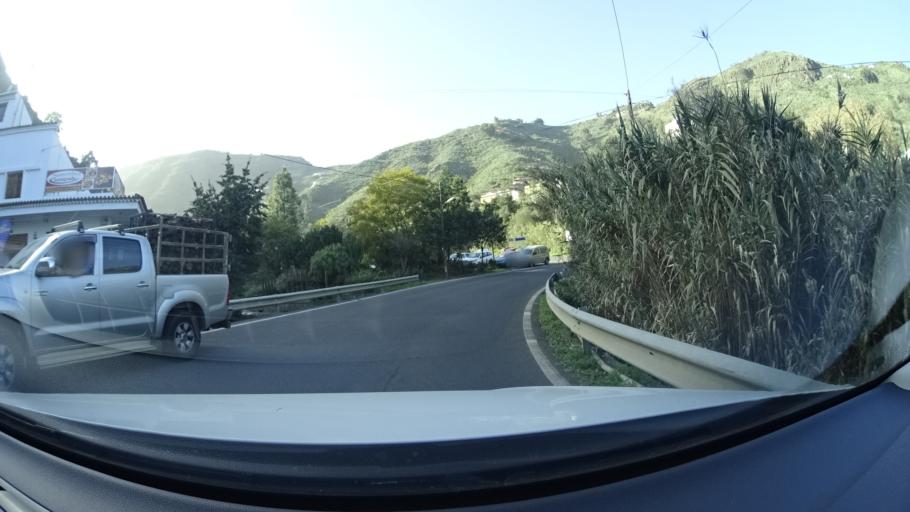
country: ES
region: Canary Islands
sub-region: Provincia de Las Palmas
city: Vega de San Mateo
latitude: 28.0174
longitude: -15.5556
